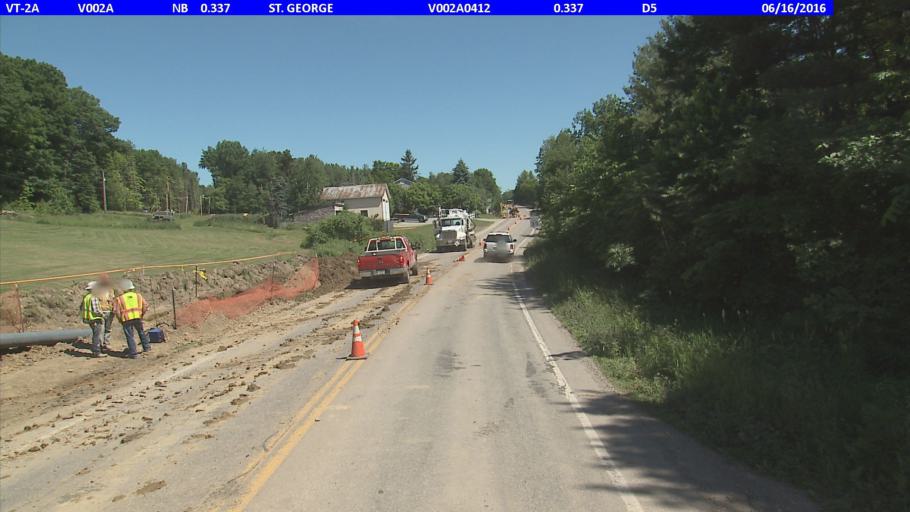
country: US
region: Vermont
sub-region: Chittenden County
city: Hinesburg
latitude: 44.3744
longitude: -73.1272
